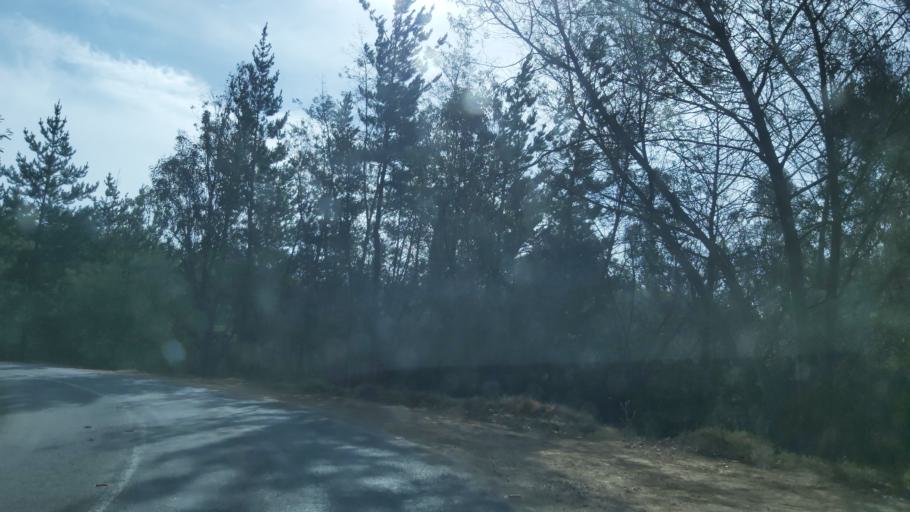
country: CL
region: Maule
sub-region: Provincia de Talca
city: Constitucion
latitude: -34.8539
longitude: -72.0288
